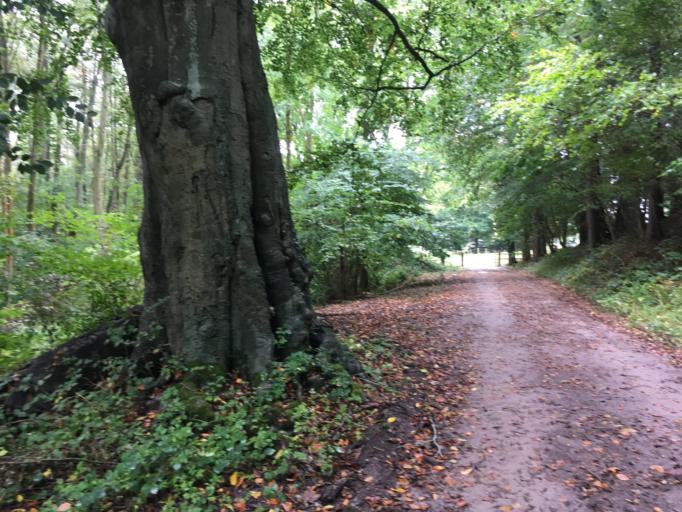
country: GB
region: England
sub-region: South Gloucestershire
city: Falfield
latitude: 51.6283
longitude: -2.4483
